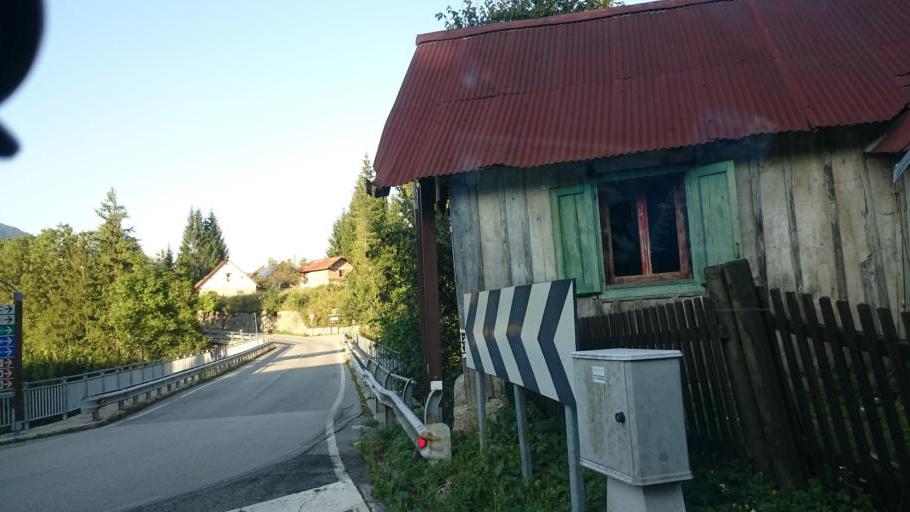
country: IT
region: Friuli Venezia Giulia
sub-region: Provincia di Udine
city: Tarvisio
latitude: 46.5019
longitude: 13.5927
